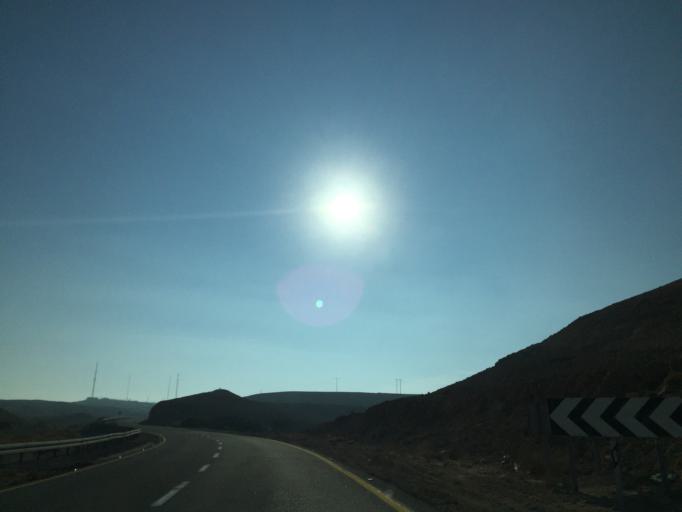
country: JO
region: Ma'an
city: Al Quwayrah
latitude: 30.0259
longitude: 35.0468
